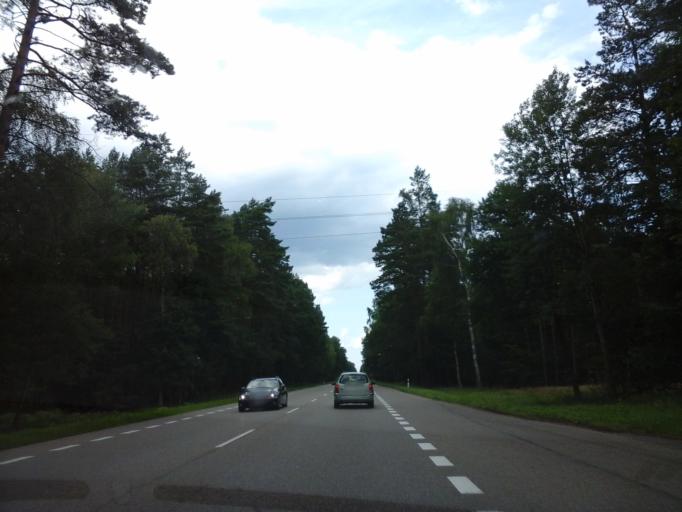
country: PL
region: West Pomeranian Voivodeship
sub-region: Powiat goleniowski
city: Goleniow
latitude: 53.6553
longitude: 14.8158
